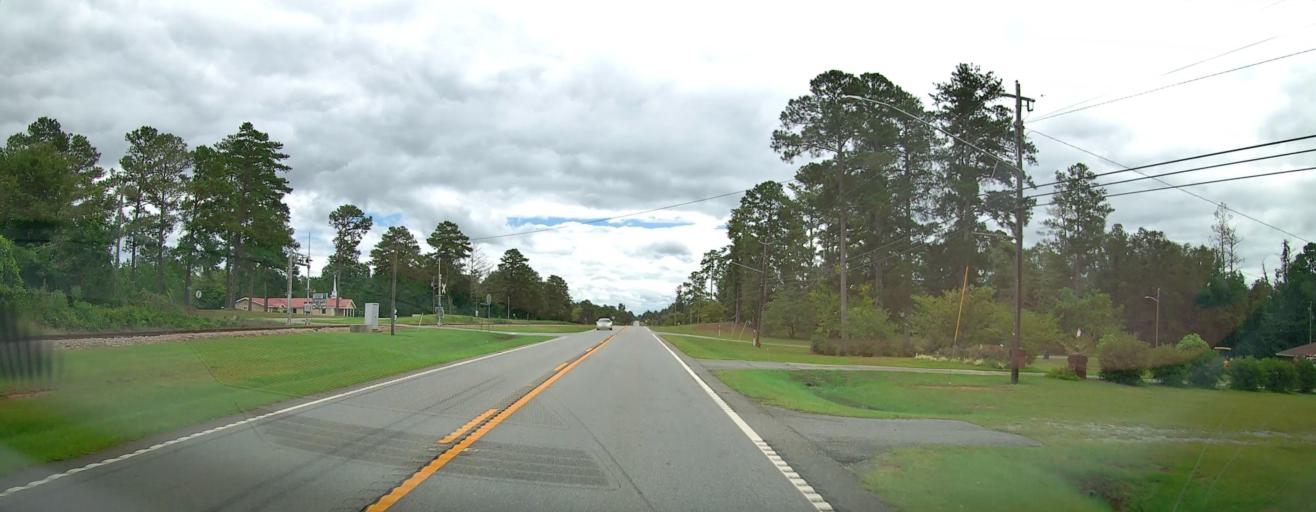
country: US
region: Georgia
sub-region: Twiggs County
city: Jeffersonville
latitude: 32.6801
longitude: -83.3374
